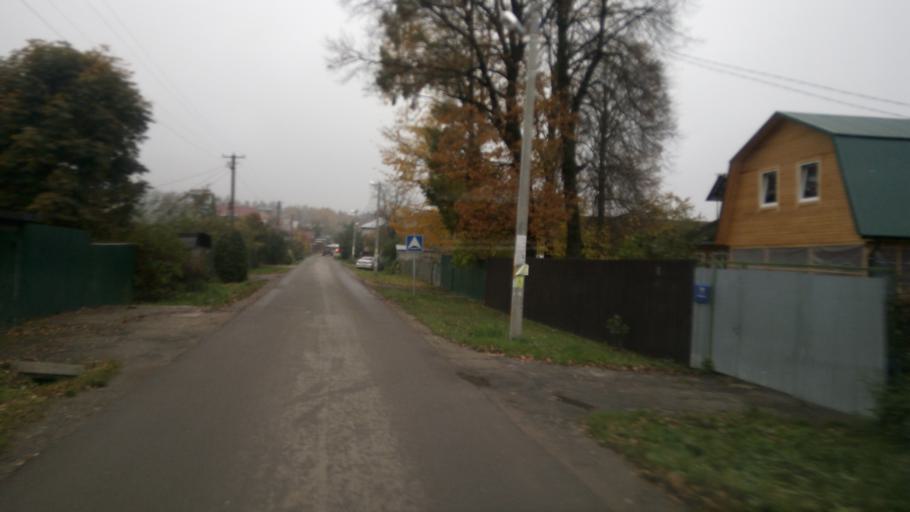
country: RU
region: Moskovskaya
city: Firsanovka
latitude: 55.9310
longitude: 37.2589
